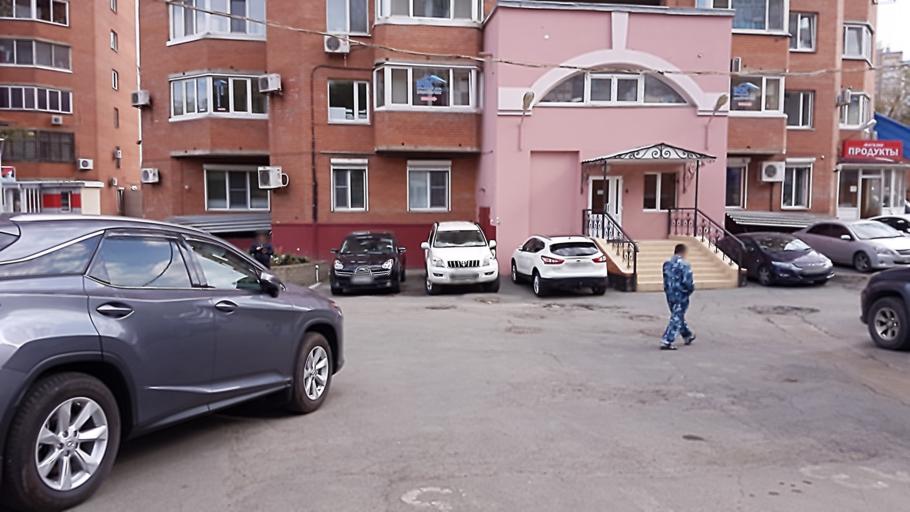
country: RU
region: Primorskiy
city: Vladivostok
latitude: 43.1290
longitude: 131.9088
